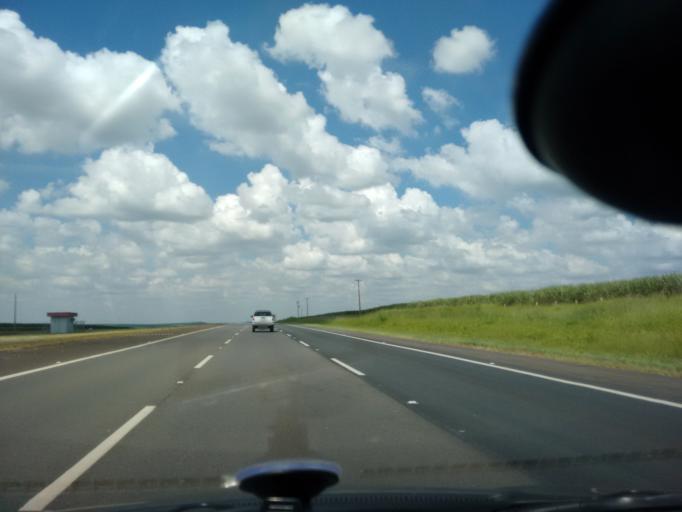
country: BR
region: Sao Paulo
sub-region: Santa Barbara D'Oeste
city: Santa Barbara d'Oeste
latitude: -22.7876
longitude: -47.4252
